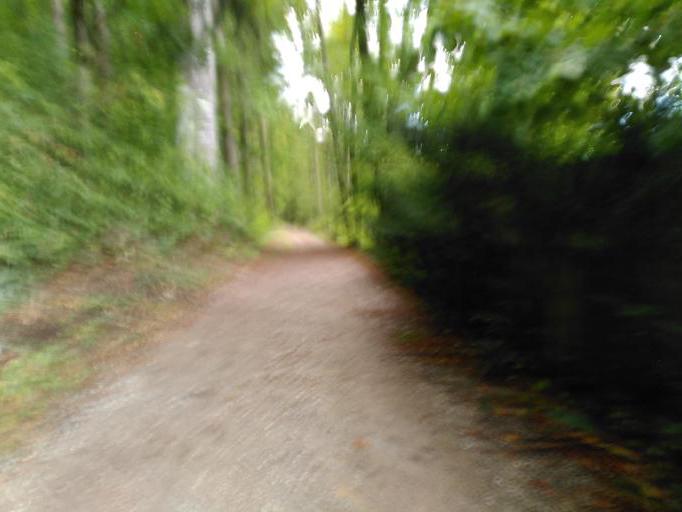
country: CH
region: Bern
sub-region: Emmental District
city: Ersigen
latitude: 47.0930
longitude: 7.6094
